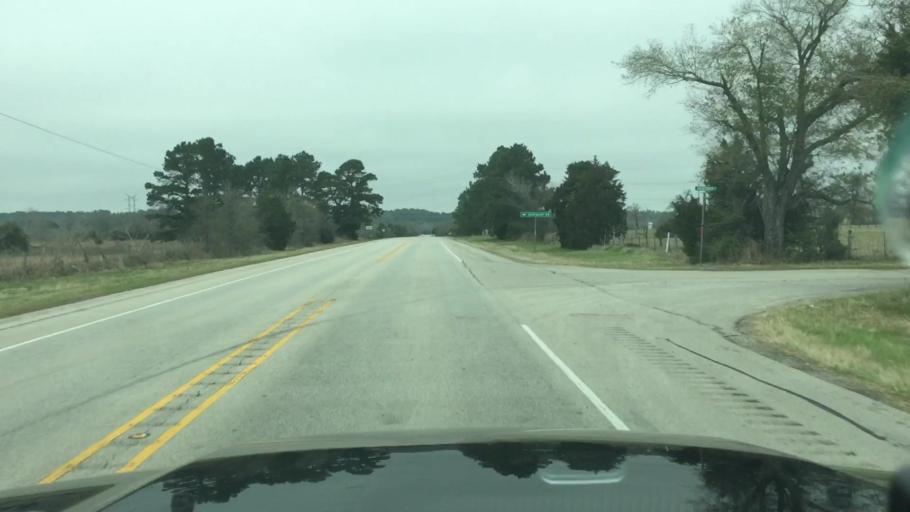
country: US
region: Texas
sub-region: Fayette County
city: La Grange
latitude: 30.0249
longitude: -96.9025
